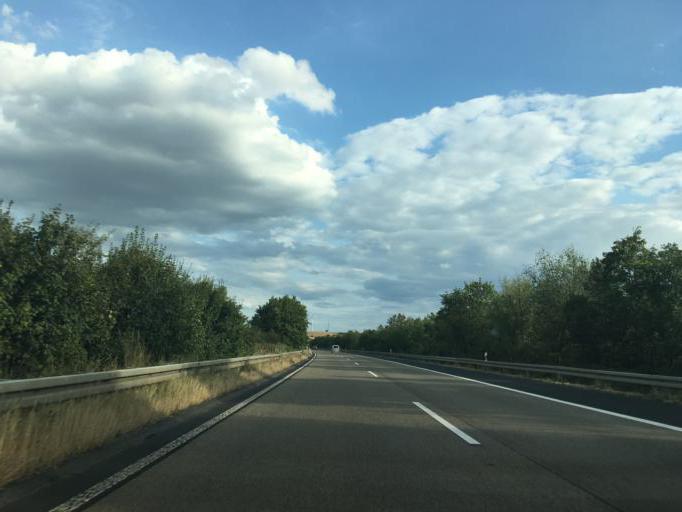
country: DE
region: Hesse
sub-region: Regierungsbezirk Darmstadt
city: Altenstadt
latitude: 50.3289
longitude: 8.9257
